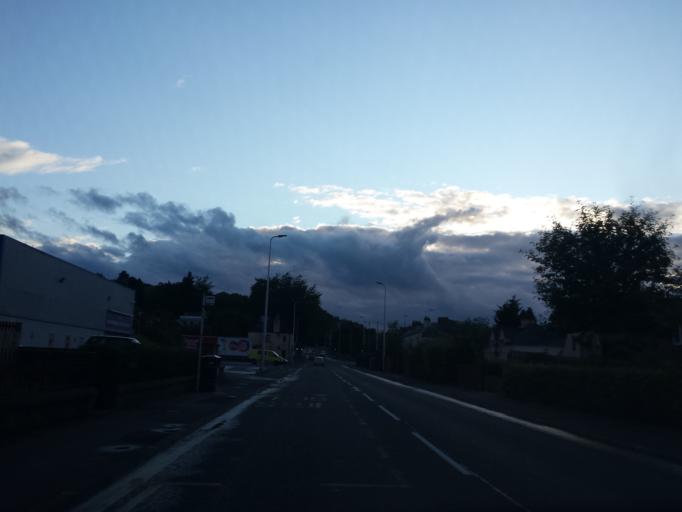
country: GB
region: Scotland
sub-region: Perth and Kinross
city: Perth
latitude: 56.4044
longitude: -3.4522
